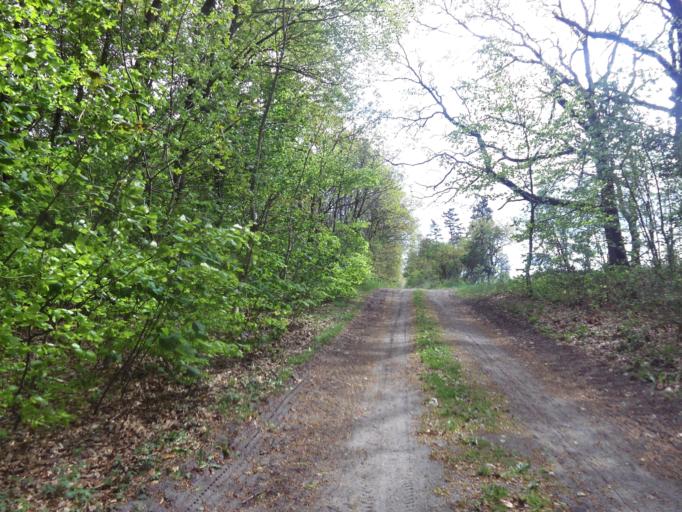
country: DK
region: South Denmark
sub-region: Tonder Kommune
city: Logumkloster
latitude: 55.0488
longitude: 8.9523
